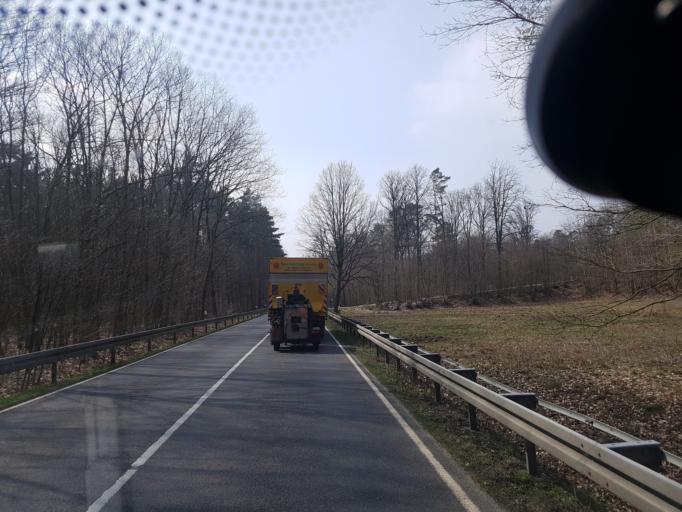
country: DE
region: Brandenburg
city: Hohenbucko
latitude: 51.7966
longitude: 13.5323
